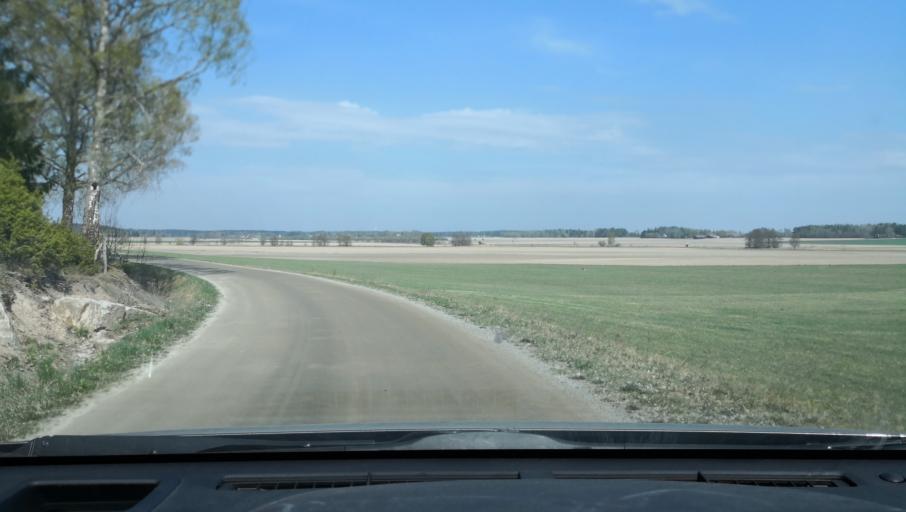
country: SE
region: Vaestmanland
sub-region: Vasteras
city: Skultuna
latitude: 59.7710
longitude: 16.4427
